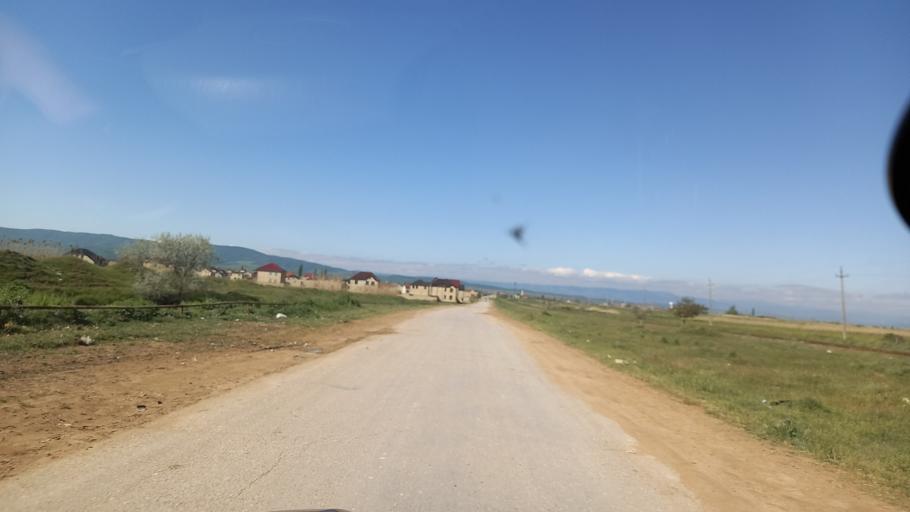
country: RU
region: Dagestan
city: Dagestanskiye Ogni
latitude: 42.1307
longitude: 48.2264
